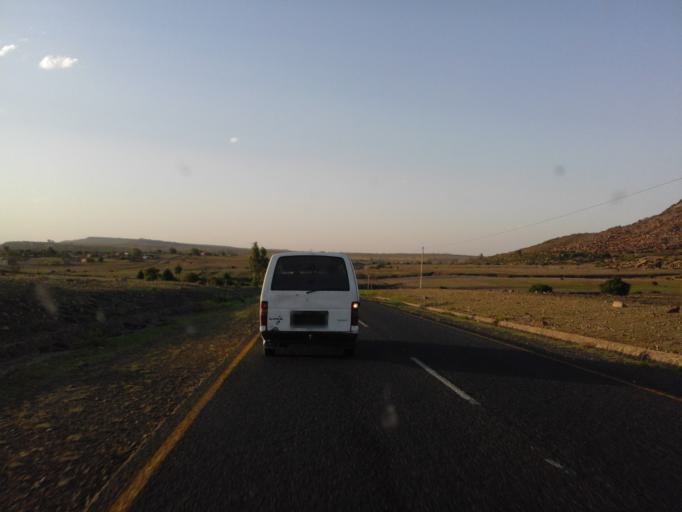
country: LS
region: Mafeteng
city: Mafeteng
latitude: -29.8785
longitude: 27.2420
